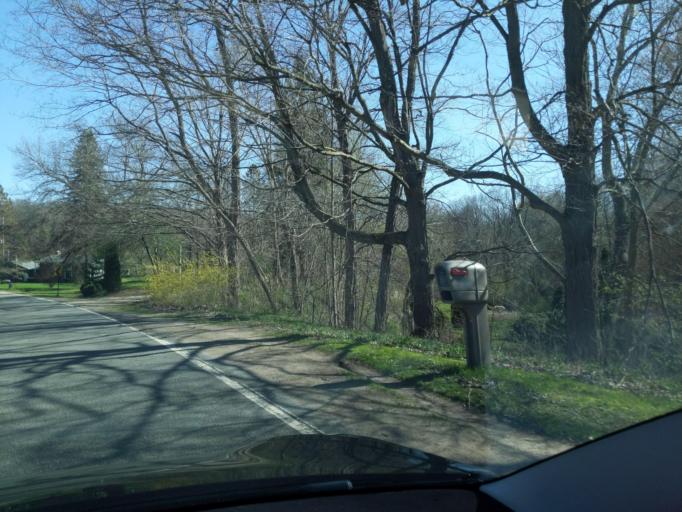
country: US
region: Michigan
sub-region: Ingham County
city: Stockbridge
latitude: 42.4381
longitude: -84.0964
